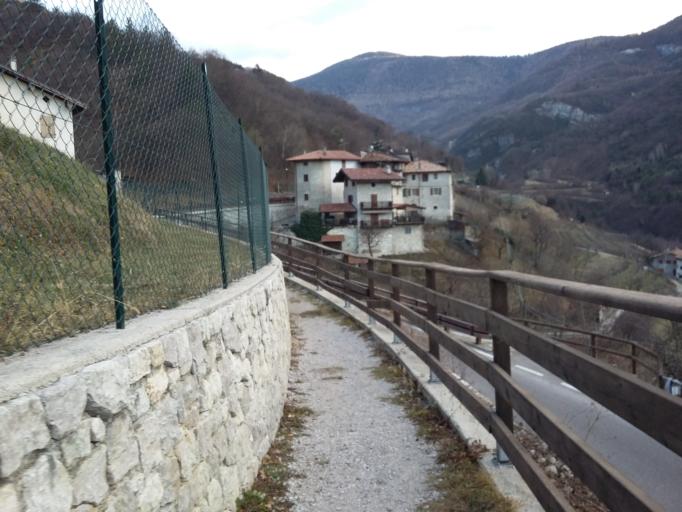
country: IT
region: Trentino-Alto Adige
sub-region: Provincia di Trento
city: Besenello
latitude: 45.9280
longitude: 11.1168
